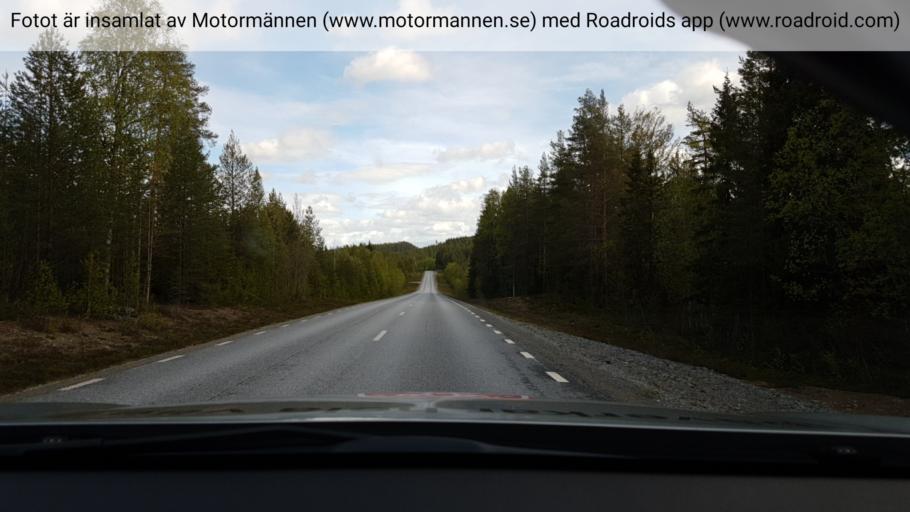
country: SE
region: Vaesterbotten
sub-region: Lycksele Kommun
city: Lycksele
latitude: 64.0451
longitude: 18.5742
